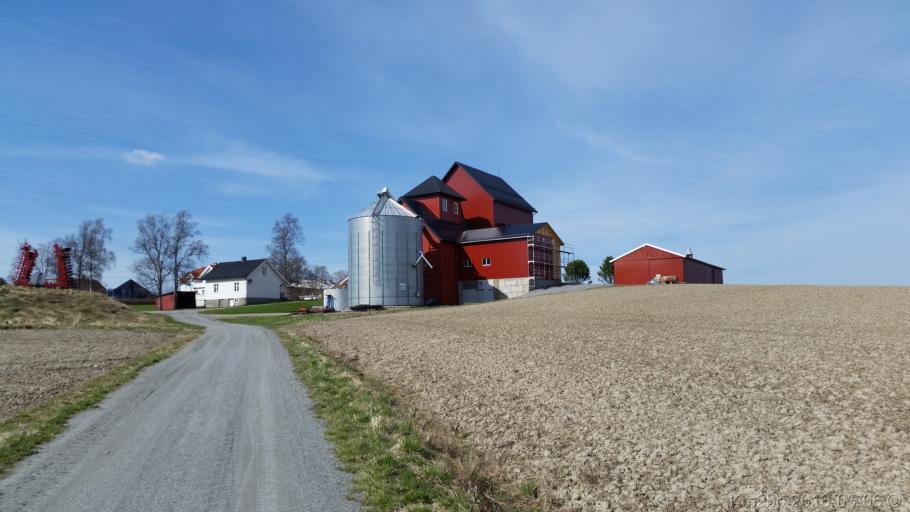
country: NO
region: Akershus
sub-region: Nes
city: Neskollen
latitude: 60.1316
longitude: 11.2892
